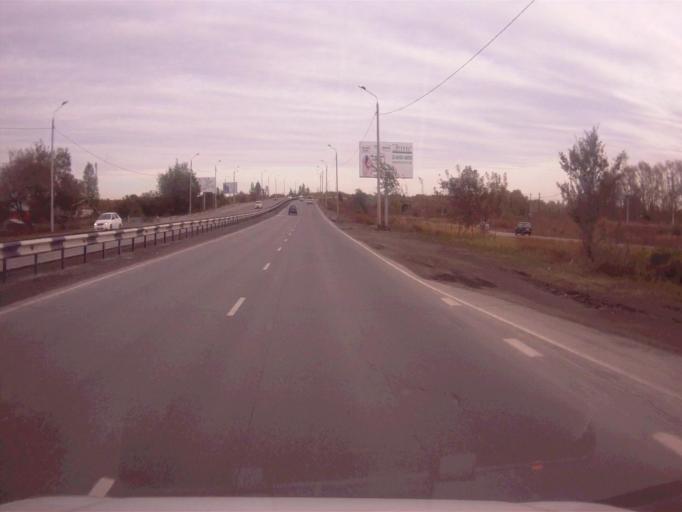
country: RU
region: Chelyabinsk
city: Novosineglazovskiy
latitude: 55.0415
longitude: 61.4328
